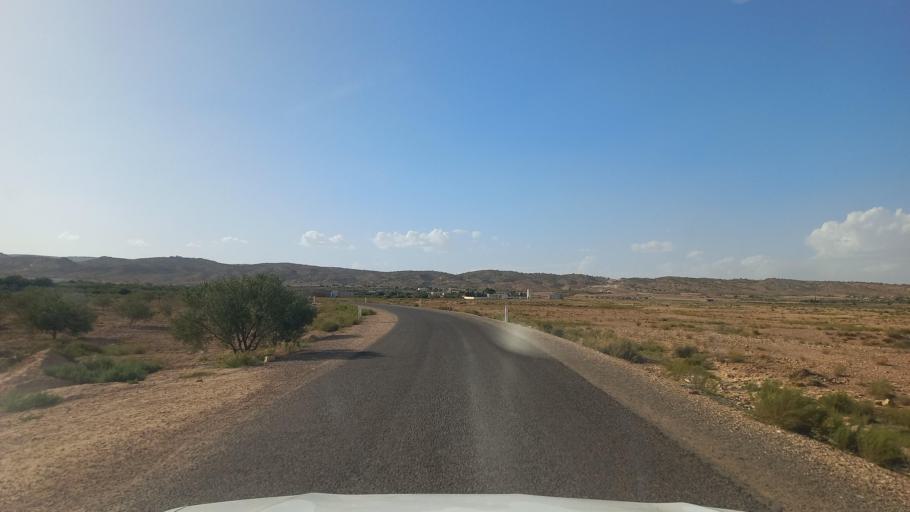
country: TN
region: Al Qasrayn
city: Sbiba
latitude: 35.3402
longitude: 8.9948
